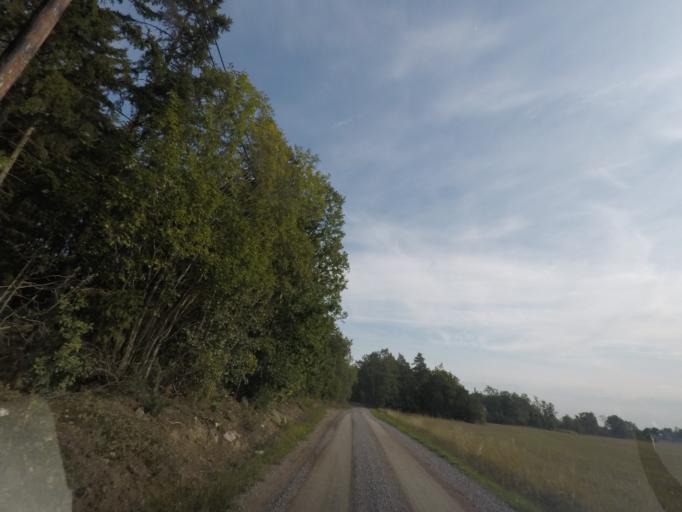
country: SE
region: Vaestmanland
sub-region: Hallstahammars Kommun
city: Kolback
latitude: 59.4815
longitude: 16.1910
